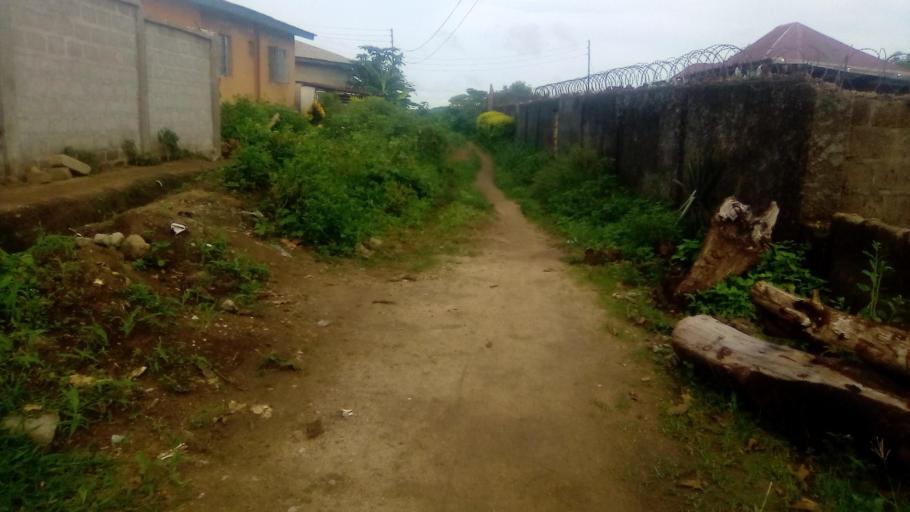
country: SL
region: Southern Province
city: Bo
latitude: 7.9761
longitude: -11.7643
